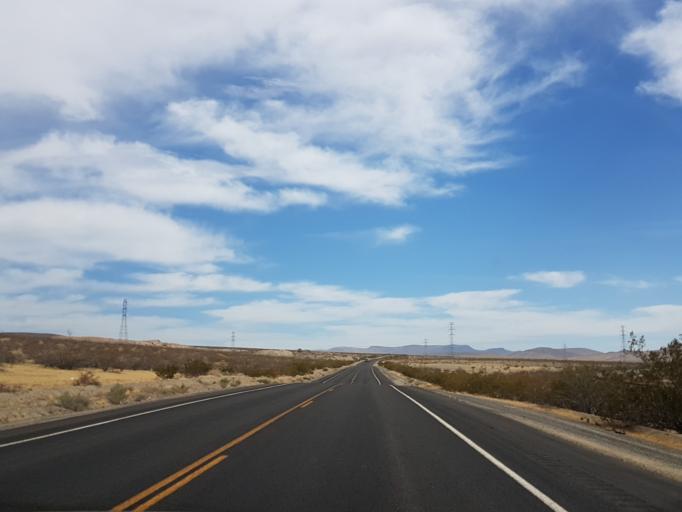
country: US
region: California
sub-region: Kern County
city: Ridgecrest
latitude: 35.4265
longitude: -117.7064
